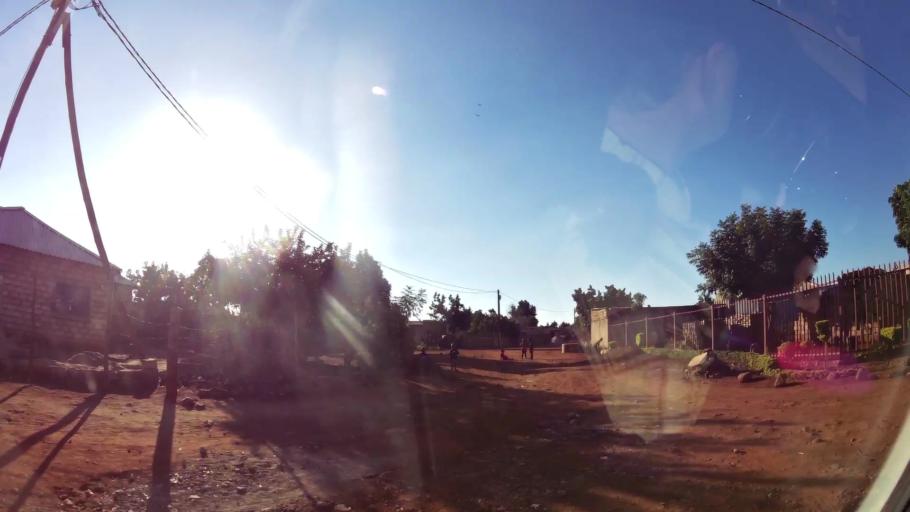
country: ZA
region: Limpopo
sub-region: Waterberg District Municipality
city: Mokopane
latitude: -24.1837
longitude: 28.9807
